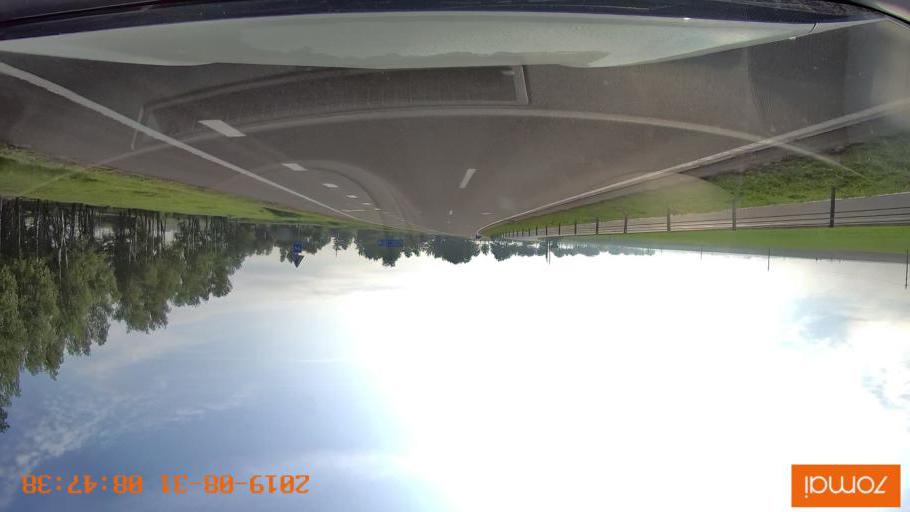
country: BY
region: Minsk
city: Luhavaya Slabada
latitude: 53.7651
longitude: 27.8676
